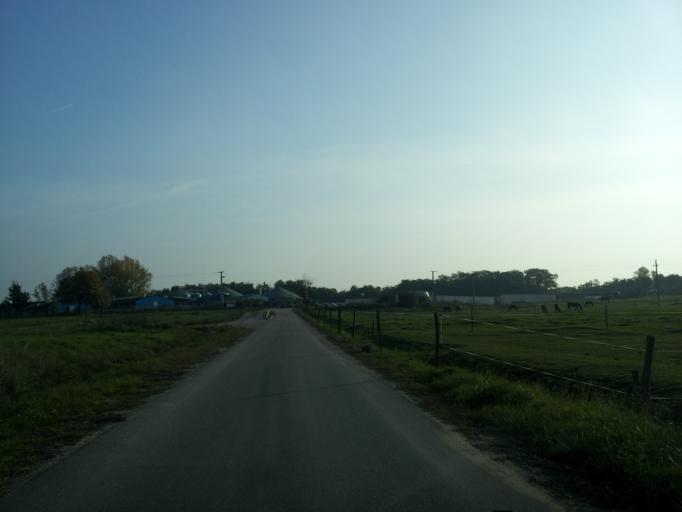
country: HU
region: Komarom-Esztergom
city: Kisber
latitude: 47.4900
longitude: 18.0478
